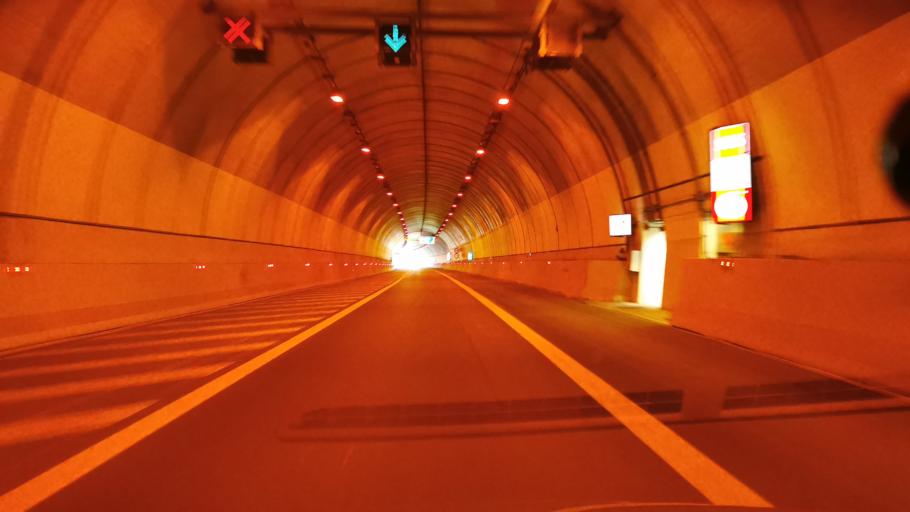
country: IT
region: Piedmont
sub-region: Provincia di Cuneo
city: Cuneo
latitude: 44.4273
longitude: 7.5672
